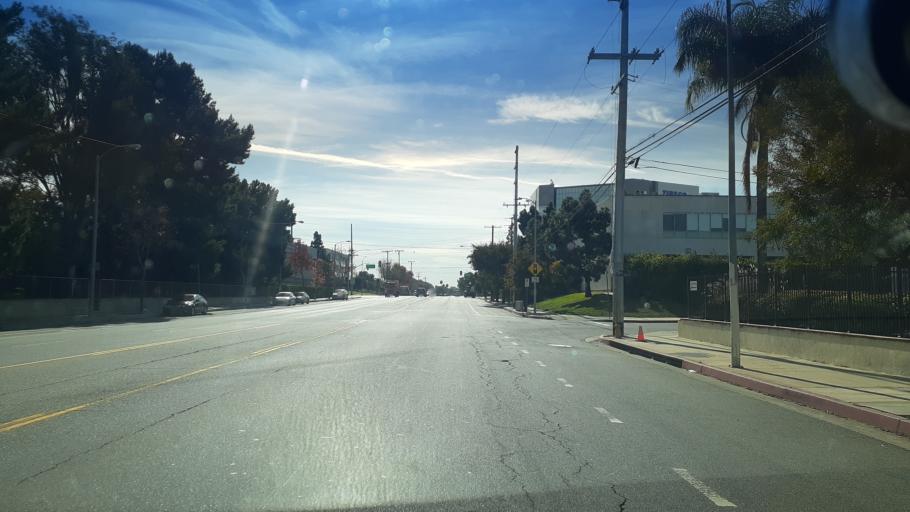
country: US
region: California
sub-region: Los Angeles County
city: West Rancho Dominguez
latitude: 33.8645
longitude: -118.2817
